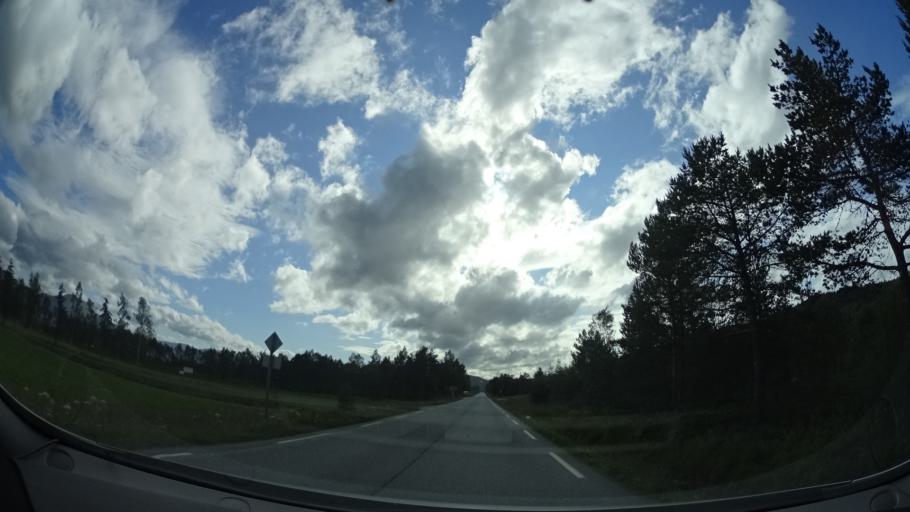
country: NO
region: More og Romsdal
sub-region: Halsa
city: Liaboen
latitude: 63.1240
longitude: 8.3418
